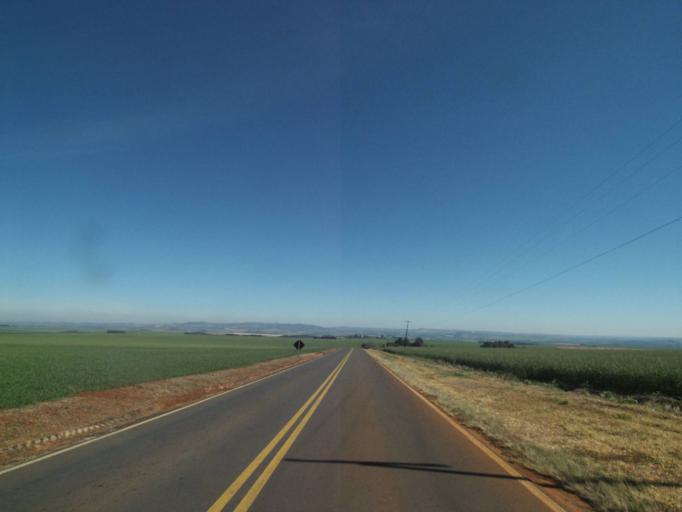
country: BR
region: Parana
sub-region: Tibagi
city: Tibagi
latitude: -24.5196
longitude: -50.3353
